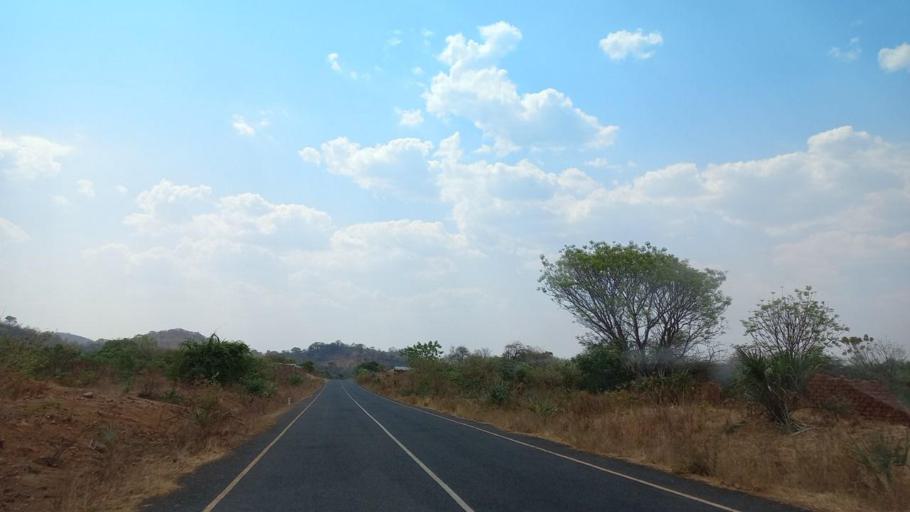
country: ZM
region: Lusaka
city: Luangwa
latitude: -15.3195
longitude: 30.3363
